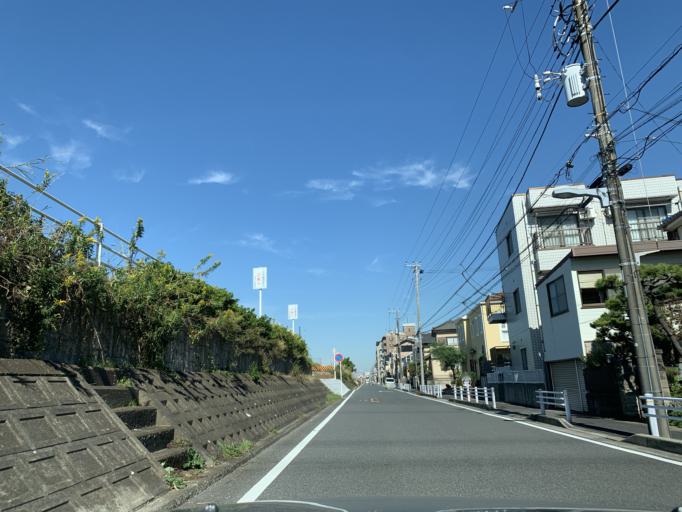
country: JP
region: Tokyo
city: Urayasu
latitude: 35.6473
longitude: 139.8855
